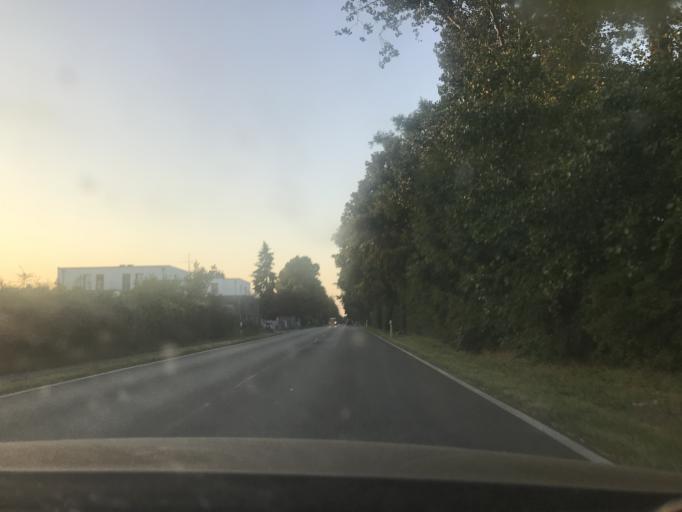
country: DE
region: North Rhine-Westphalia
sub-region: Regierungsbezirk Dusseldorf
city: Moers
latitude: 51.4814
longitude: 6.6327
